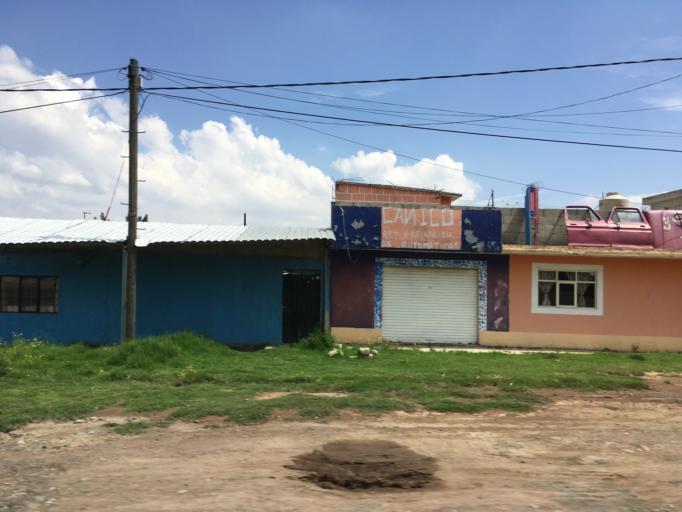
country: MX
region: Mexico
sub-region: Timilpan
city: Tercera Manzana de Zaragoza
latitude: 19.8734
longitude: -99.6904
